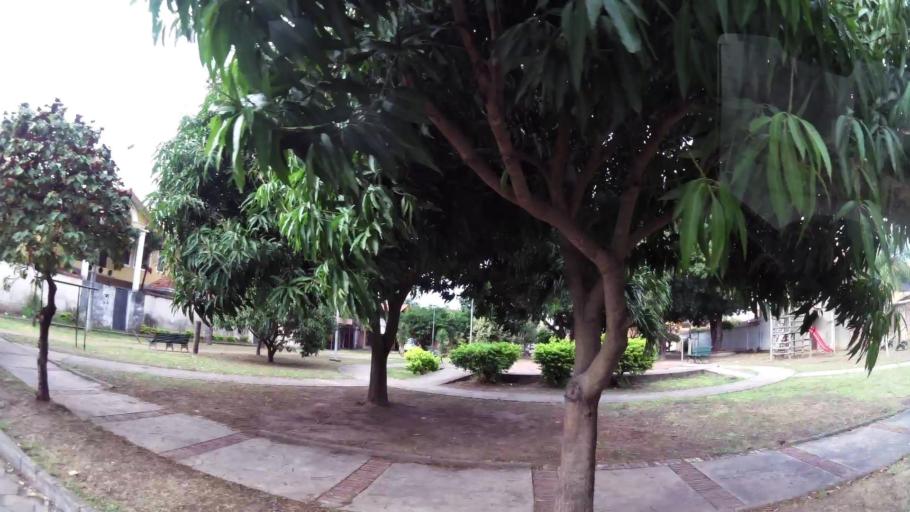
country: BO
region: Santa Cruz
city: Santa Cruz de la Sierra
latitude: -17.7528
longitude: -63.1688
